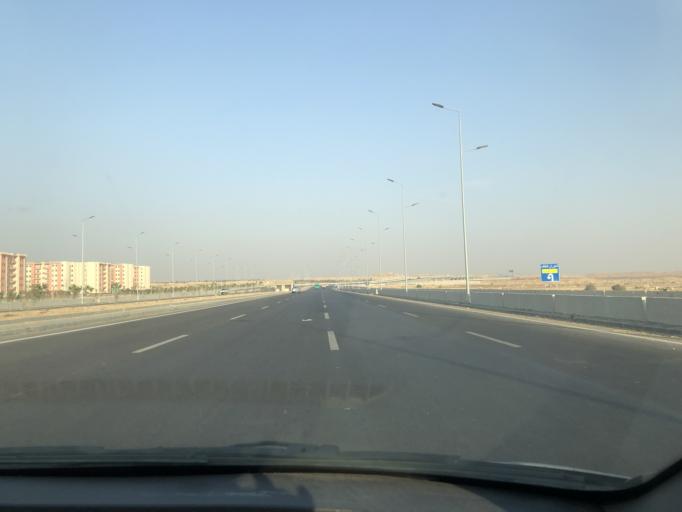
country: EG
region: Al Jizah
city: Madinat Sittah Uktubar
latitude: 29.9051
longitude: 30.9737
